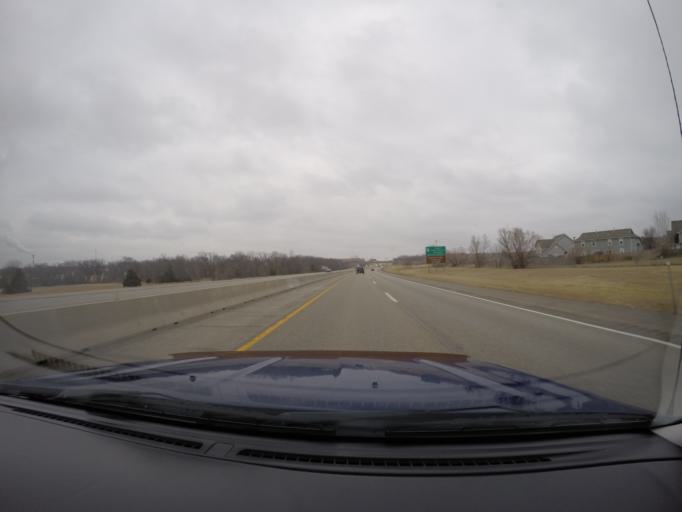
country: US
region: Kansas
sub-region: Douglas County
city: Lawrence
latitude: 38.9970
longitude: -95.2854
